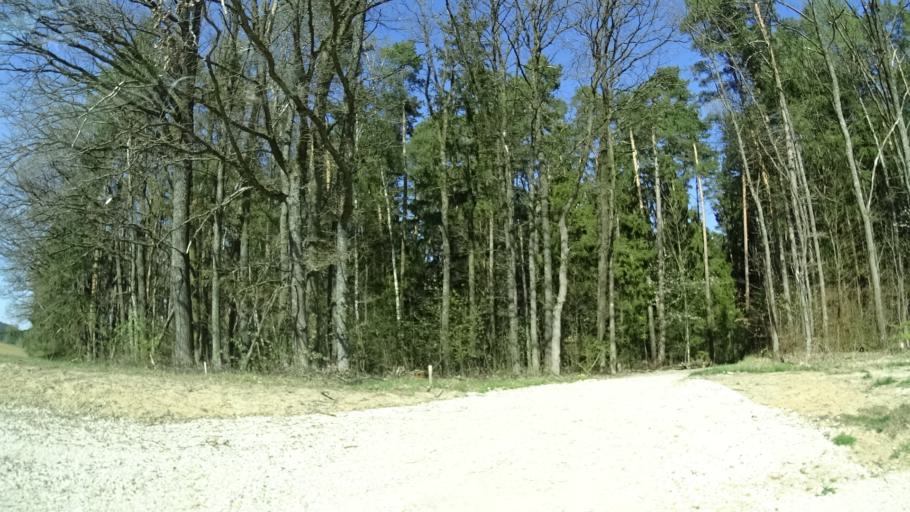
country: DE
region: Bavaria
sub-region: Upper Palatinate
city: Edelsfeld
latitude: 49.5521
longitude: 11.7112
